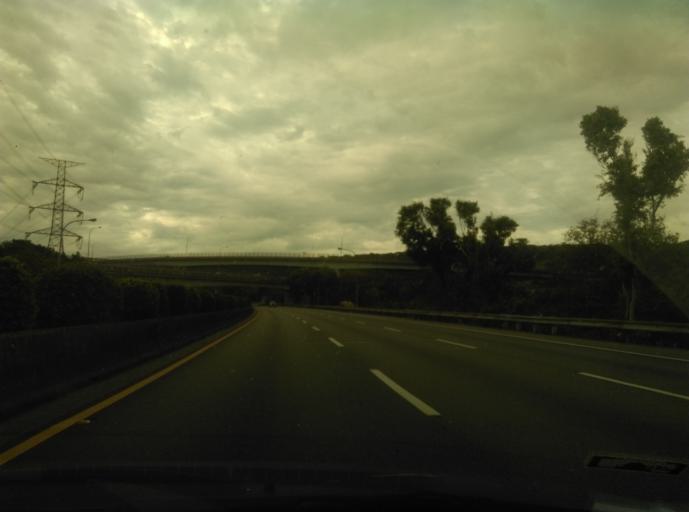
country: TW
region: Taiwan
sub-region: Taoyuan
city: Taoyuan
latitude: 24.9396
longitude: 121.3273
